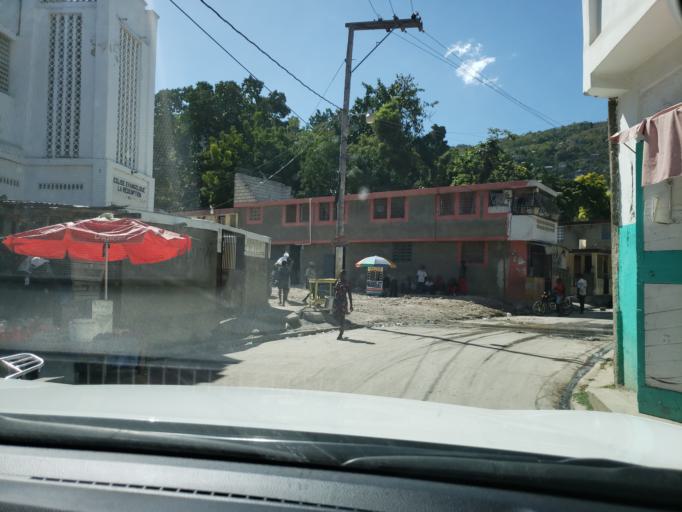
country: HT
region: Nippes
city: Miragoane
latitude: 18.4426
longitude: -73.0908
